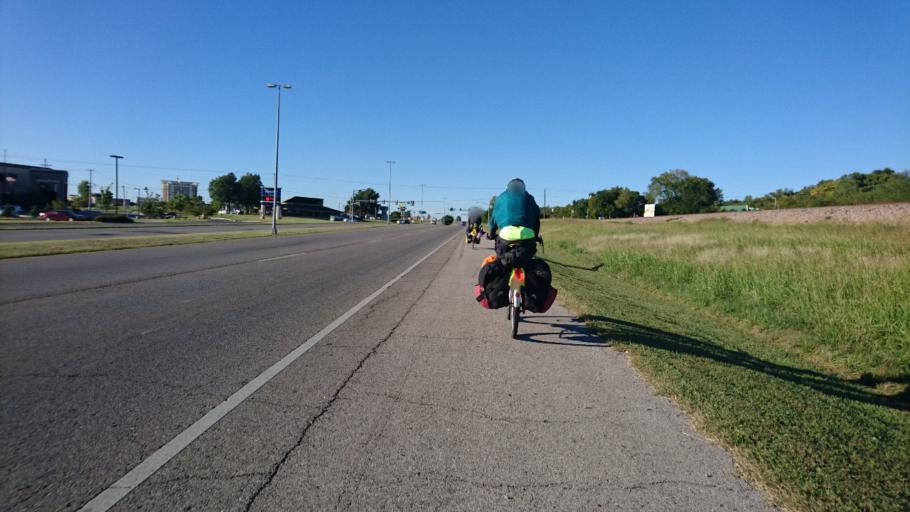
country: US
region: Oklahoma
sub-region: Rogers County
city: Claremore
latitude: 36.2946
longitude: -95.6299
